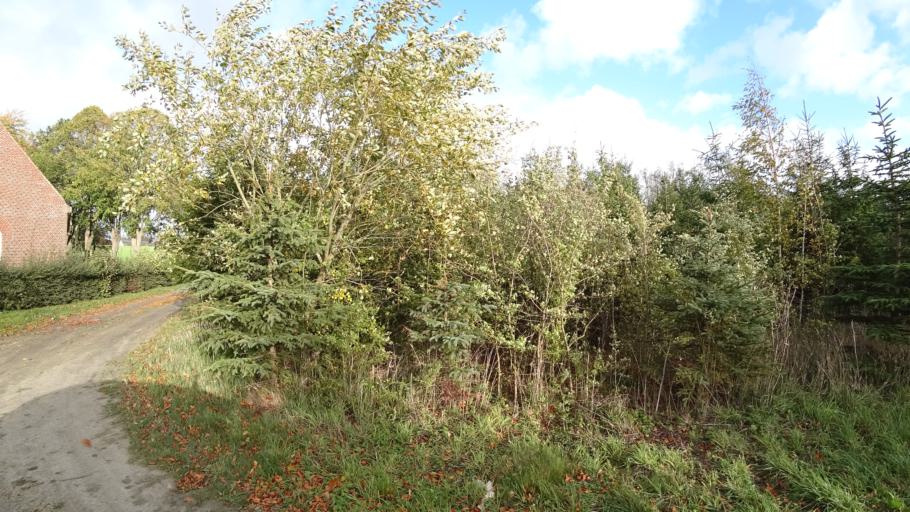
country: SE
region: Skane
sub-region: Staffanstorps Kommun
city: Staffanstorp
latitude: 55.6140
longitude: 13.2049
